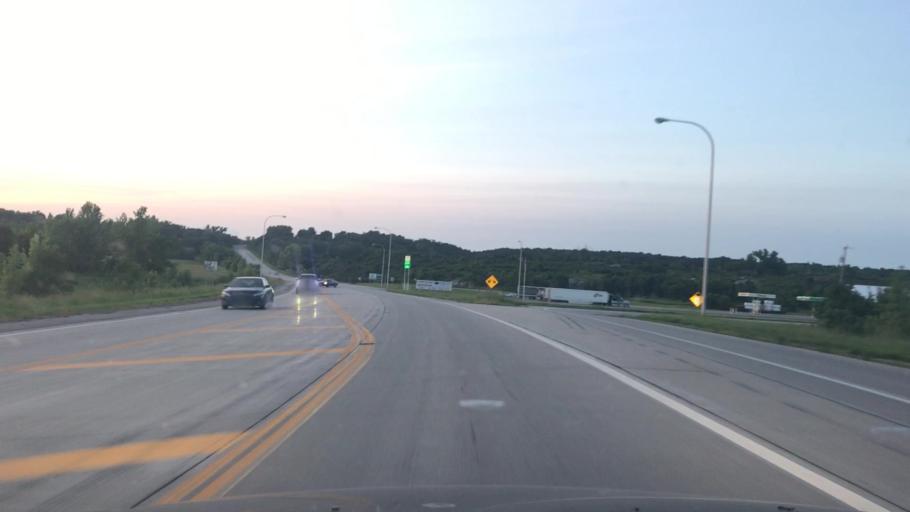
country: US
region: Minnesota
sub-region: Redwood County
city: Redwood Falls
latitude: 44.5477
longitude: -94.9946
